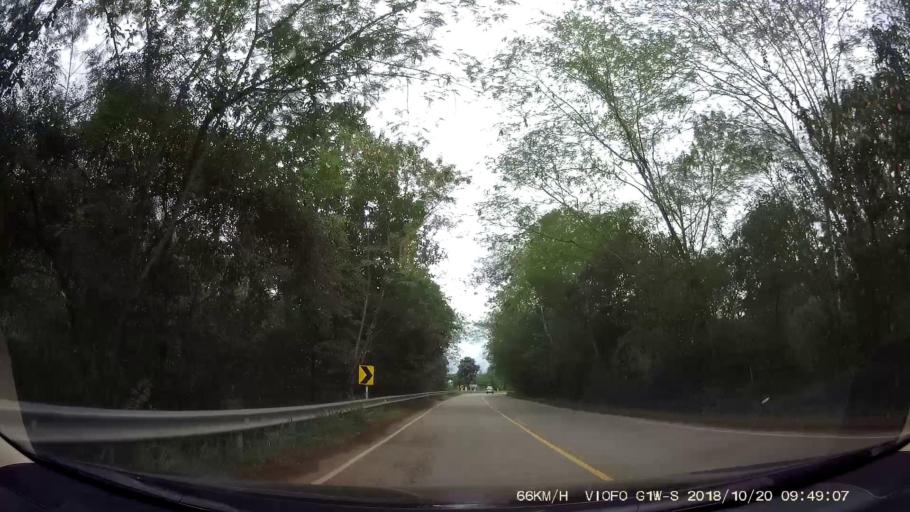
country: TH
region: Chaiyaphum
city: Khon San
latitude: 16.5164
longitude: 101.9070
